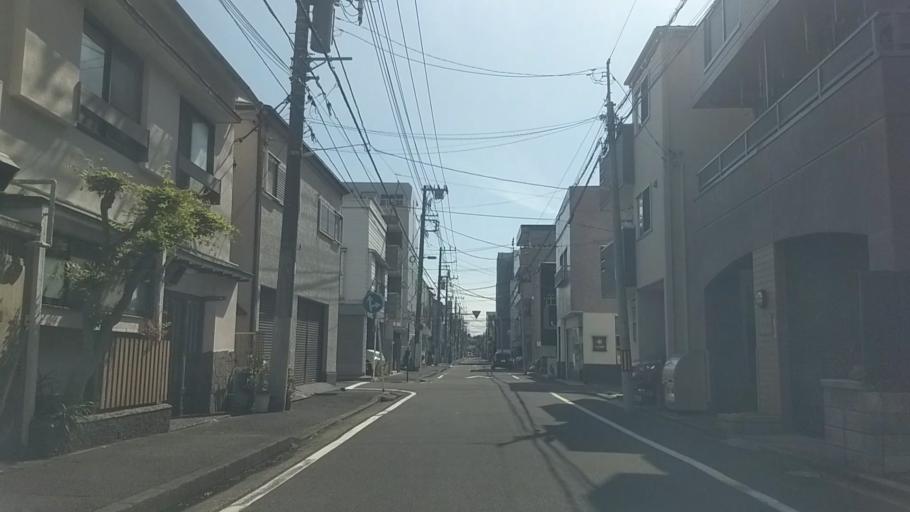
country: JP
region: Kanagawa
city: Yokohama
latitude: 35.4312
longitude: 139.6129
